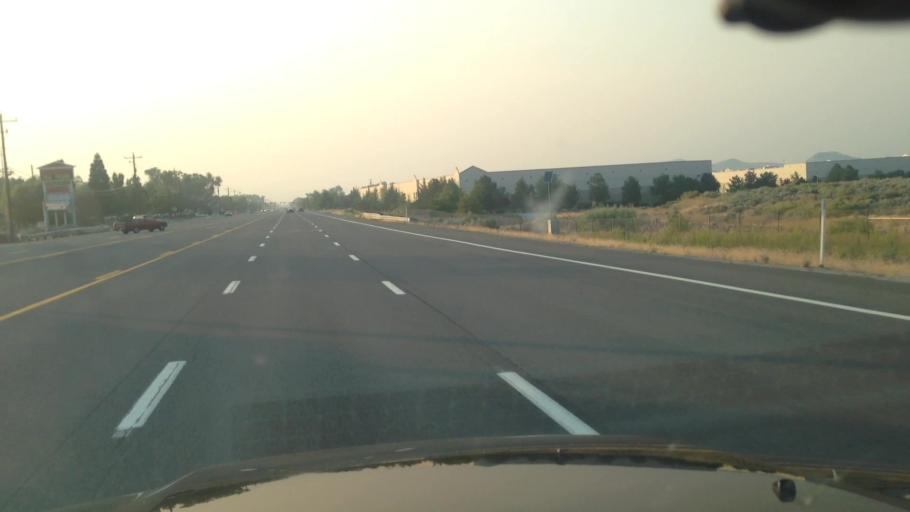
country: US
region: Nevada
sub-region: Washoe County
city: Sparks
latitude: 39.4131
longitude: -119.7527
